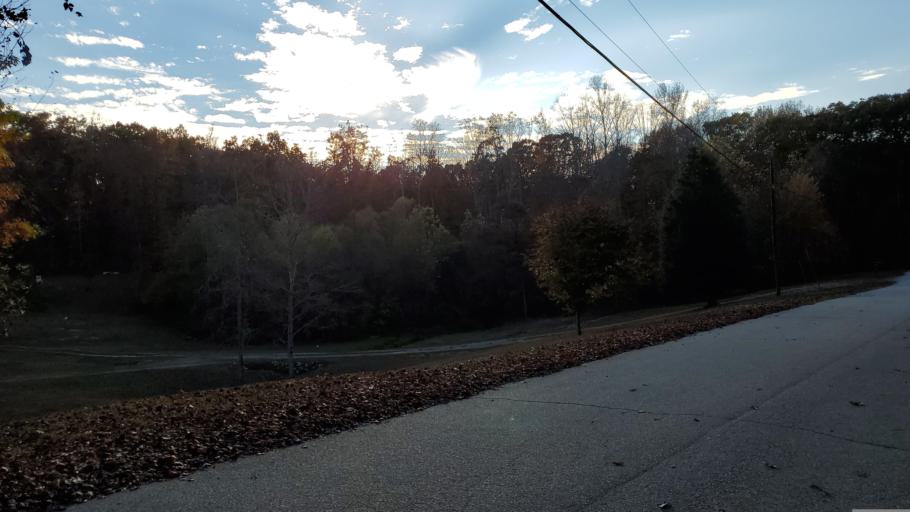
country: US
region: South Carolina
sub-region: Greenville County
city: Tigerville
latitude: 35.0698
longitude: -82.3255
